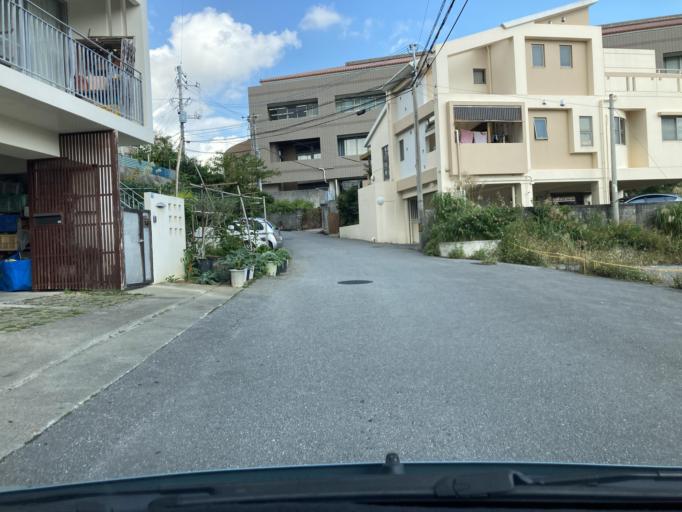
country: JP
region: Okinawa
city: Ginowan
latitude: 26.2448
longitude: 127.7263
